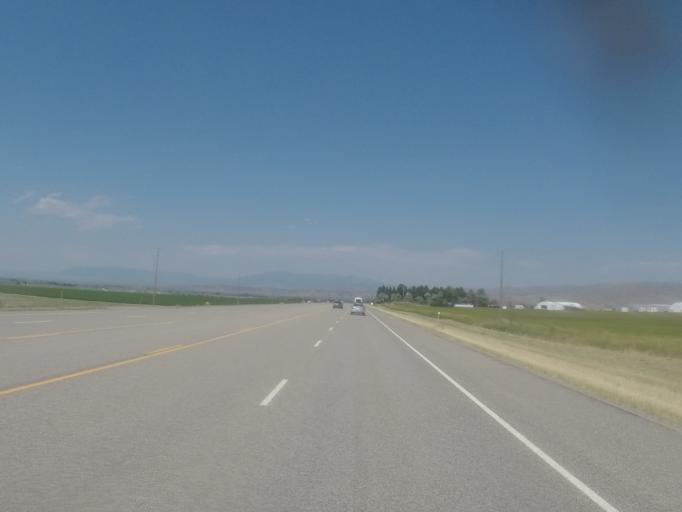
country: US
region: Montana
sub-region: Broadwater County
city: Townsend
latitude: 46.1372
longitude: -111.4806
